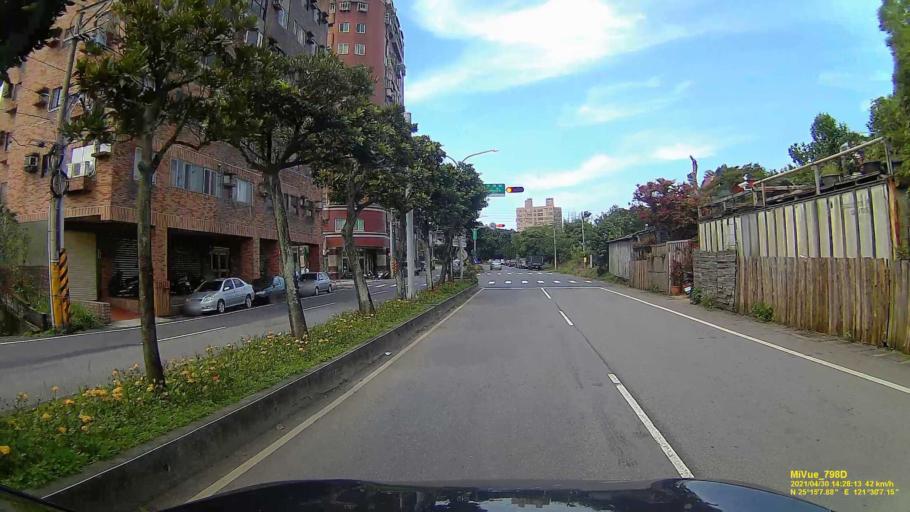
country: TW
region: Taipei
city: Taipei
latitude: 25.2523
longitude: 121.5021
